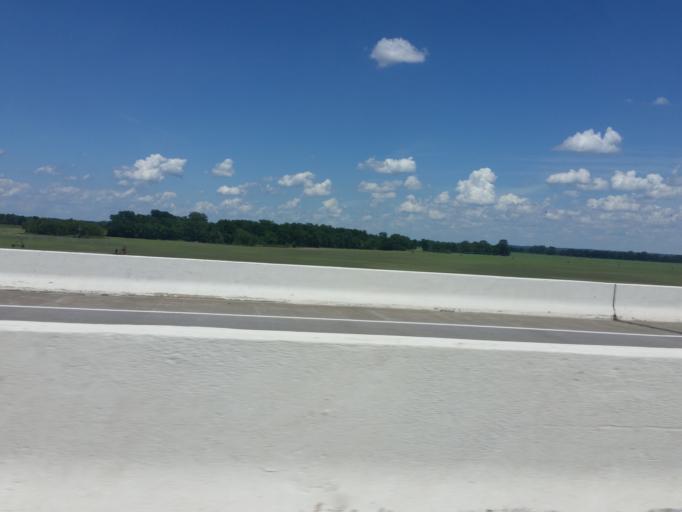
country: US
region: Missouri
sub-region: Pemiscot County
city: Caruthersville
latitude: 36.1065
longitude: -89.6082
